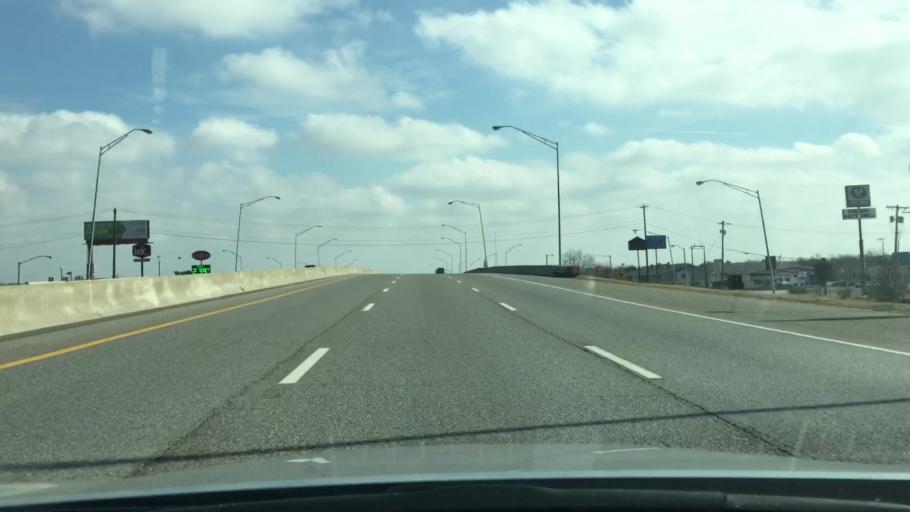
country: US
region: Oklahoma
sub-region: Oklahoma County
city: Oklahoma City
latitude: 35.3942
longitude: -97.5672
